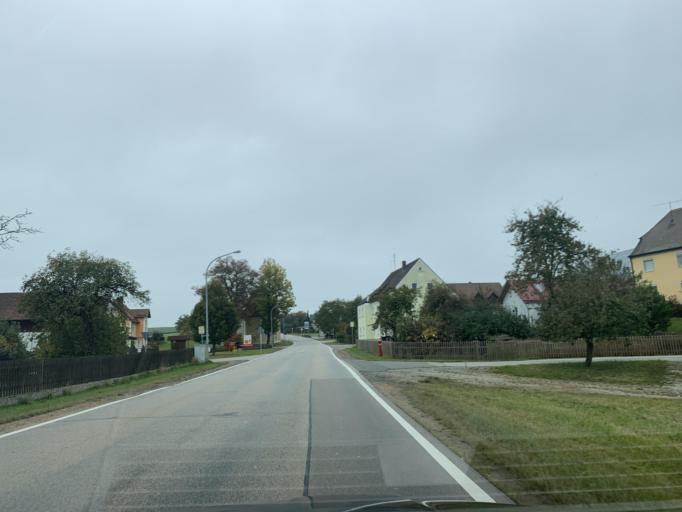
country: DE
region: Bavaria
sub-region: Upper Palatinate
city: Guteneck
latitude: 49.4545
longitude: 12.2532
